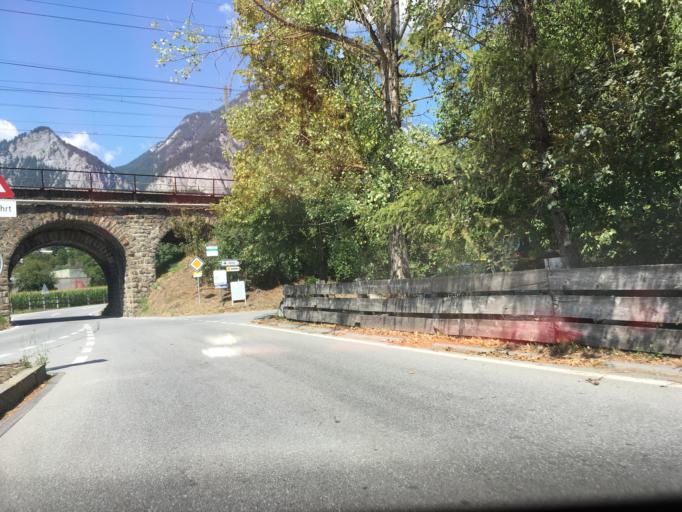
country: CH
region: Grisons
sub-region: Imboden District
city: Tamins
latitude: 46.8224
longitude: 9.4042
